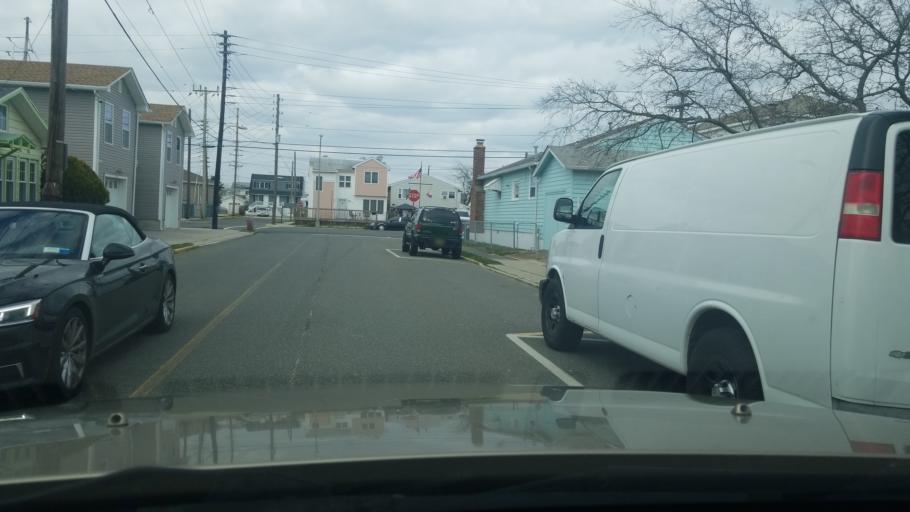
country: US
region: New Jersey
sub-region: Ocean County
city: Seaside Heights
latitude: 39.9425
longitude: -74.0772
